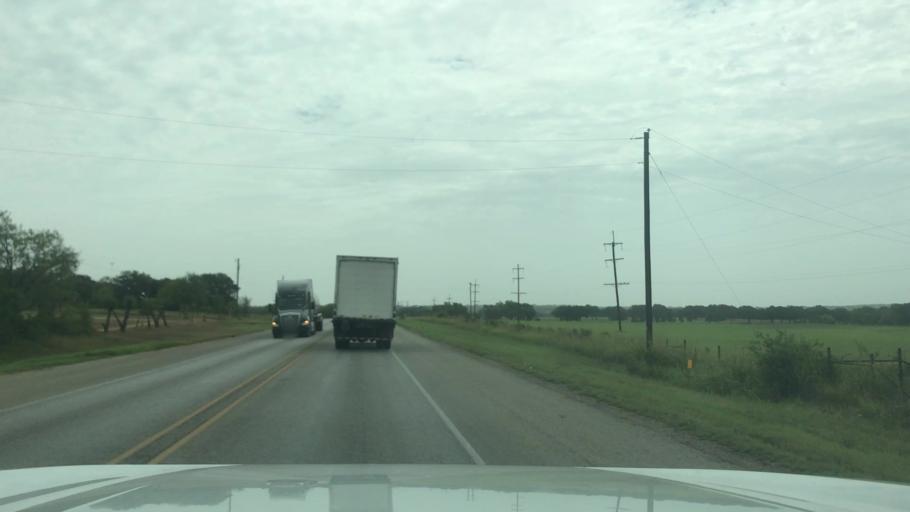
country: US
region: Texas
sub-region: Comanche County
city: De Leon
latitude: 32.0991
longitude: -98.4692
